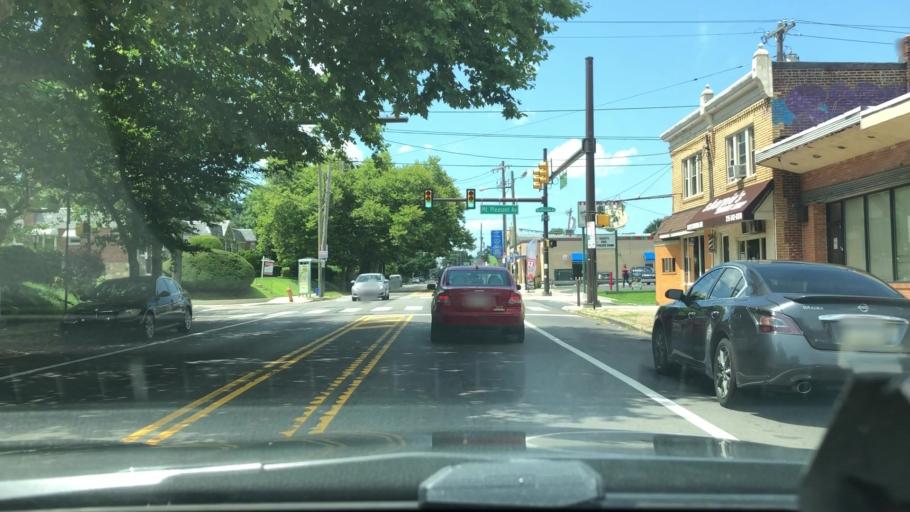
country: US
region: Pennsylvania
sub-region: Montgomery County
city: Wyndmoor
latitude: 40.0671
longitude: -75.1784
